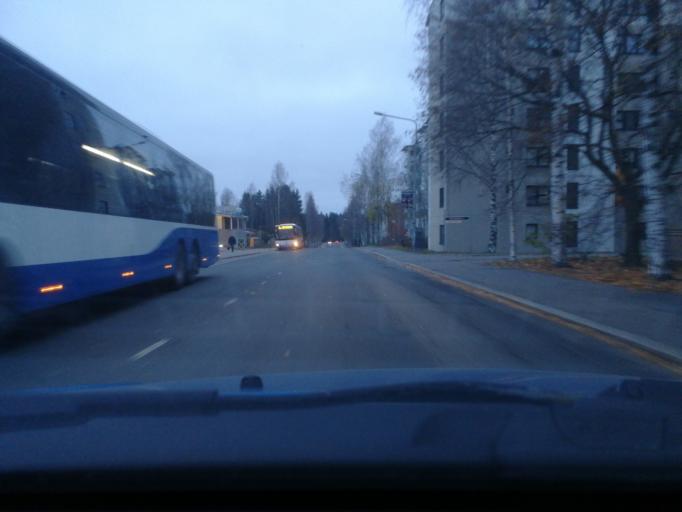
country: FI
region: Pirkanmaa
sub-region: Tampere
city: Tampere
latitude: 61.4421
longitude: 23.8522
